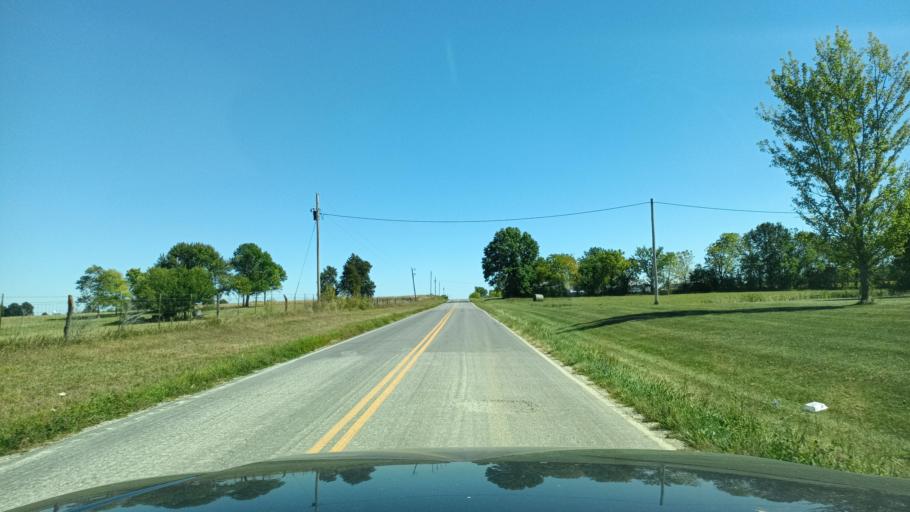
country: US
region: Missouri
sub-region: Macon County
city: La Plata
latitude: 40.0216
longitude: -92.5275
